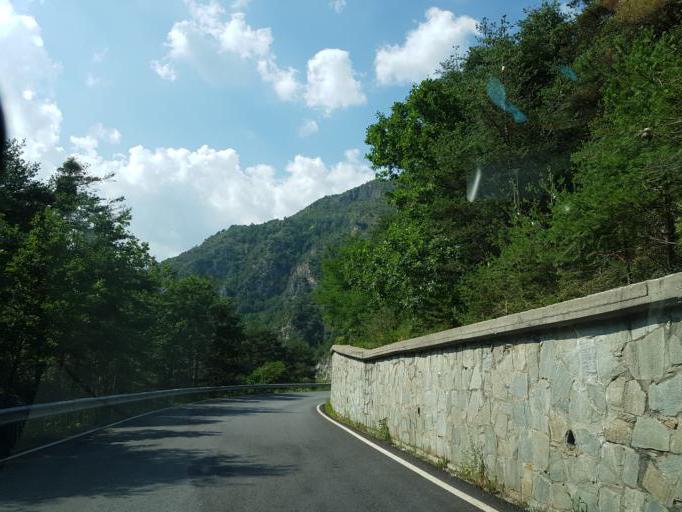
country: IT
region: Piedmont
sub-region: Provincia di Cuneo
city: Macra
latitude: 44.4975
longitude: 7.1963
